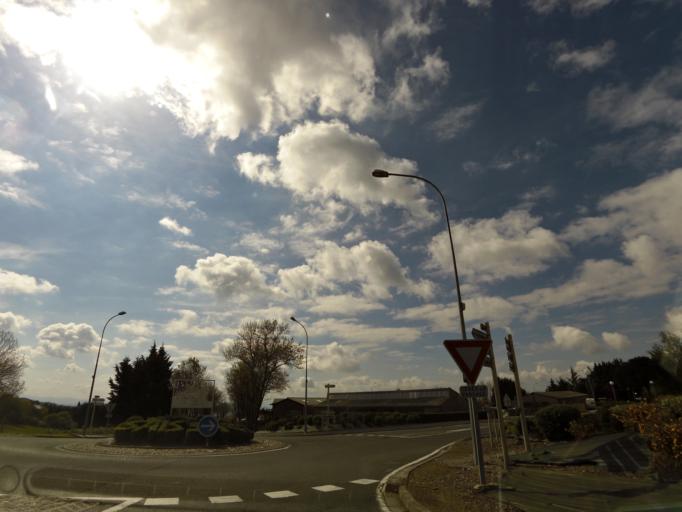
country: FR
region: Languedoc-Roussillon
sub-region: Departement de l'Aude
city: Villepinte
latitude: 43.3628
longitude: 2.1617
